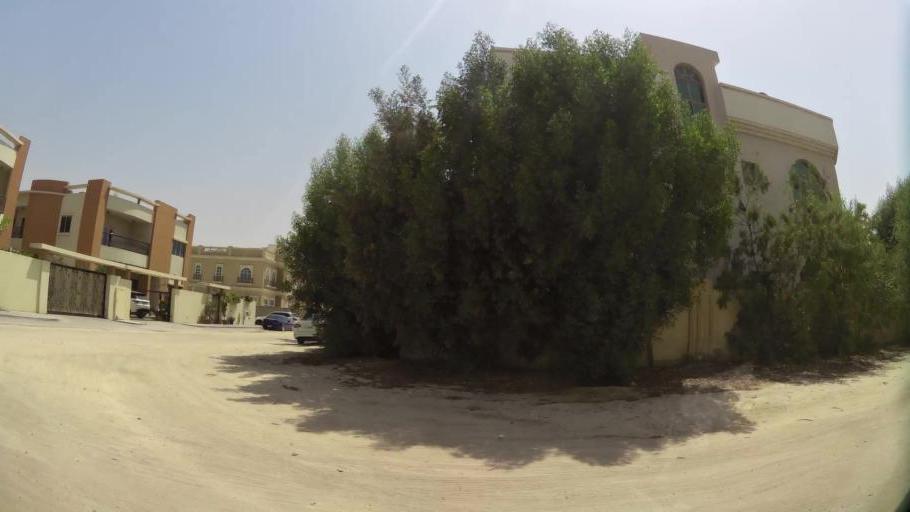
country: AE
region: Ajman
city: Ajman
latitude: 25.3932
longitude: 55.4251
